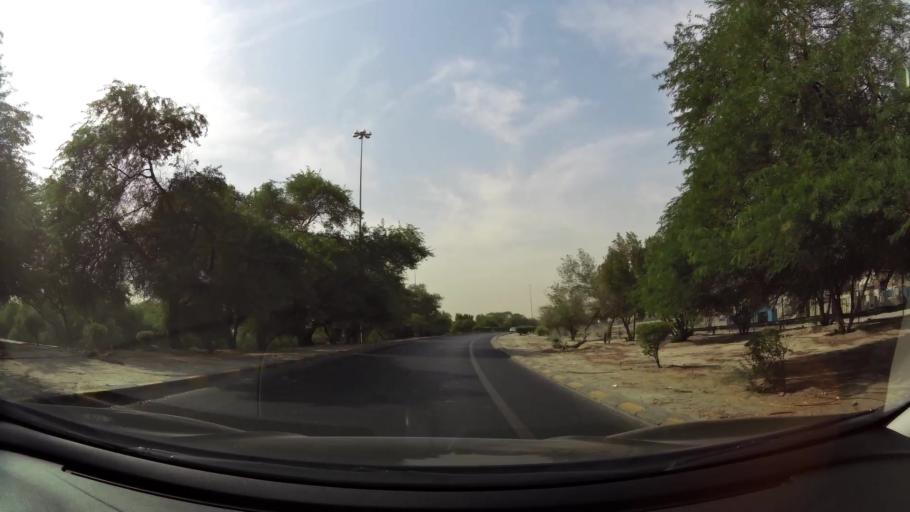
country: KW
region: Al Farwaniyah
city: Janub as Surrah
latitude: 29.2674
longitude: 47.9860
